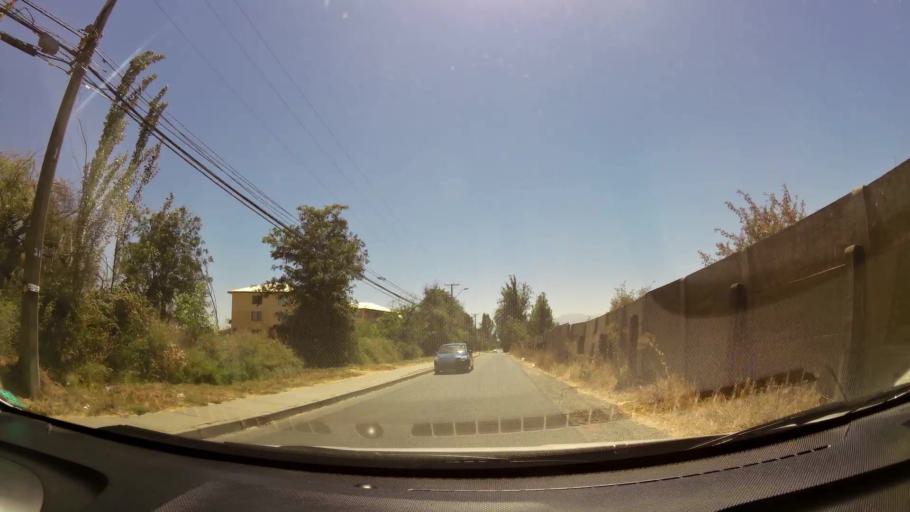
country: CL
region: O'Higgins
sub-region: Provincia de Cachapoal
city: Rancagua
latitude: -34.1587
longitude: -70.7538
